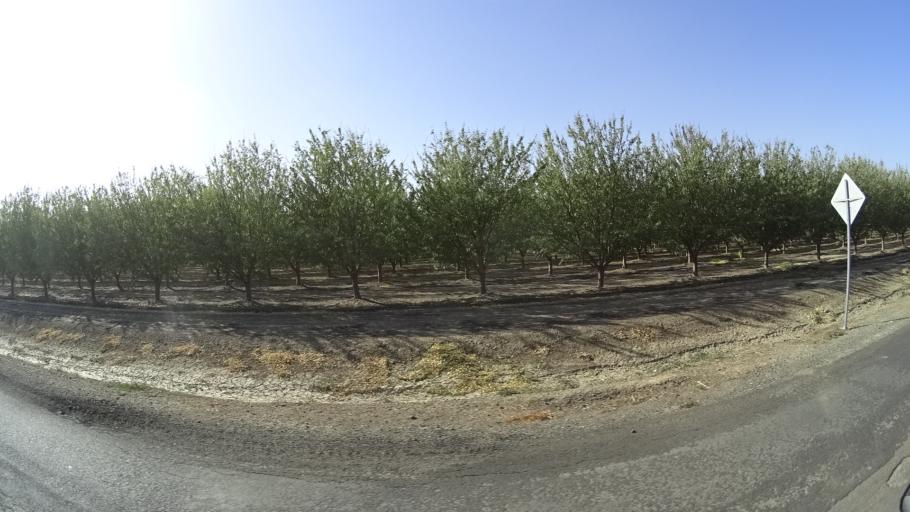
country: US
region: California
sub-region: Yolo County
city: Woodland
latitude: 38.7211
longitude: -121.8564
